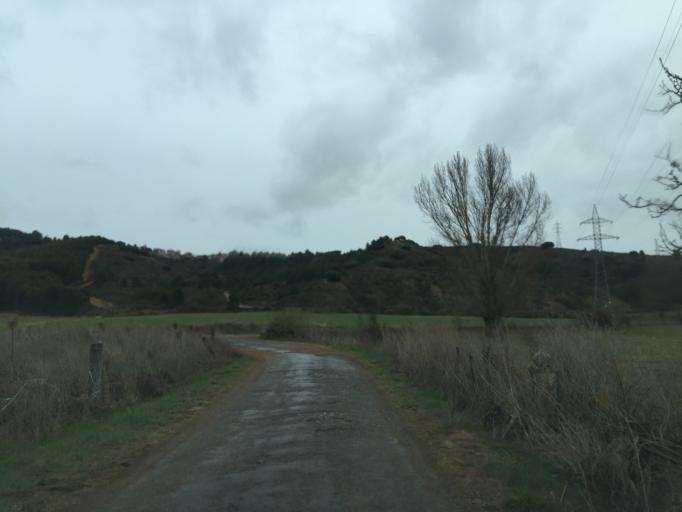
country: ES
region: Castille and Leon
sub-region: Provincia de Leon
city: Leon
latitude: 42.6008
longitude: -5.5448
